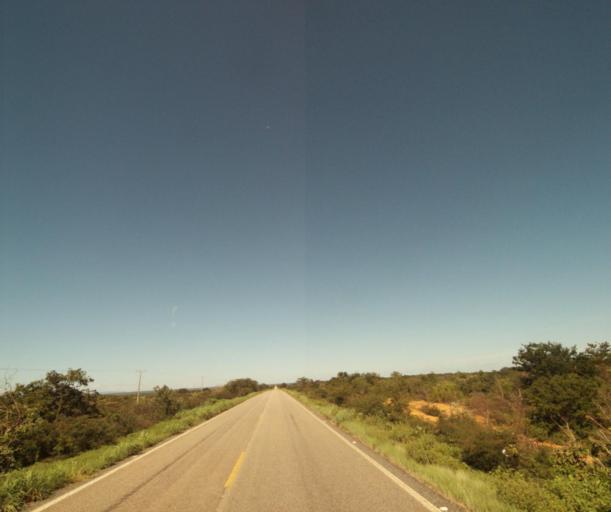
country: BR
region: Bahia
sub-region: Palmas De Monte Alto
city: Palmas de Monte Alto
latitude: -14.2558
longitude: -43.2410
